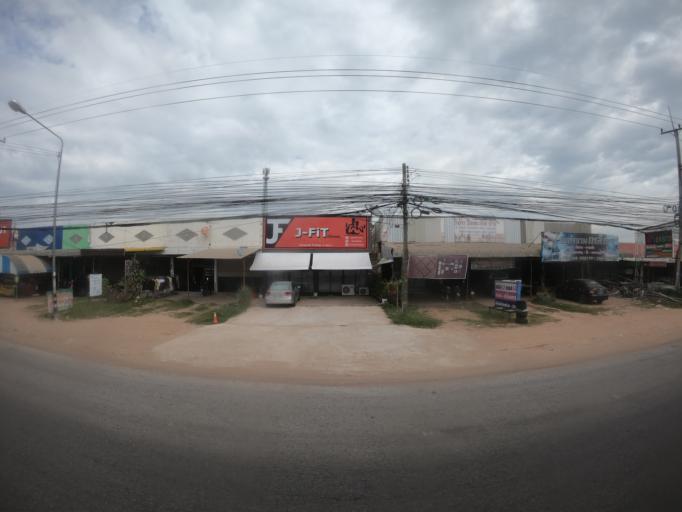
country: TH
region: Maha Sarakham
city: Maha Sarakham
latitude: 16.2144
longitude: 103.2794
